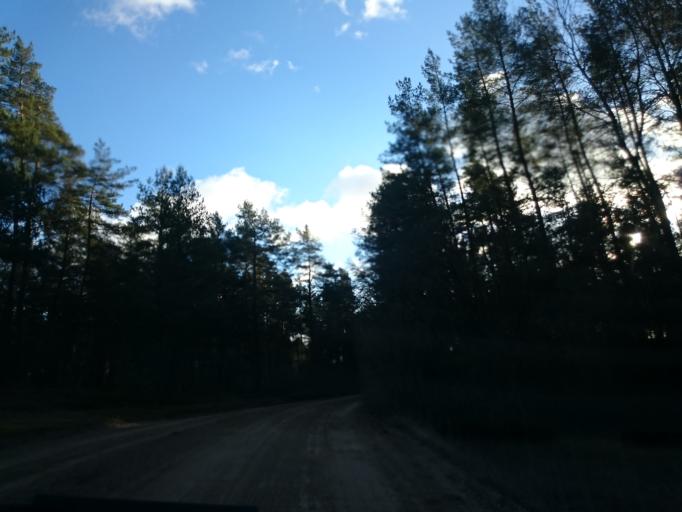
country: LV
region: Garkalne
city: Garkalne
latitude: 57.0525
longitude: 24.4161
